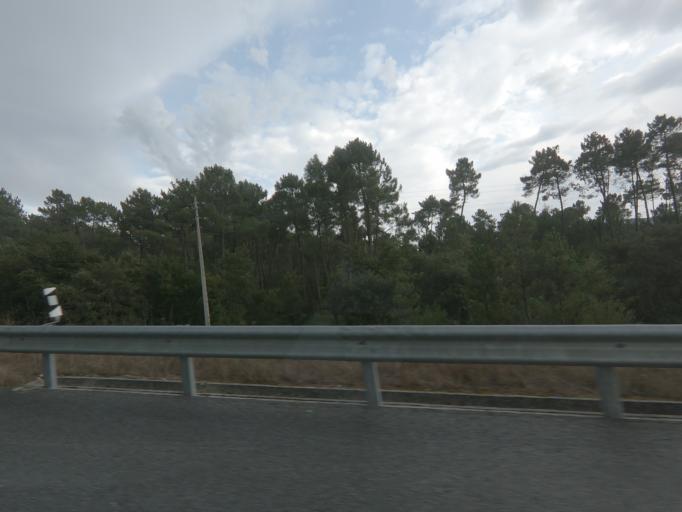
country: PT
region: Viseu
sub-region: Viseu
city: Campo
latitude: 40.7057
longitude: -7.9466
